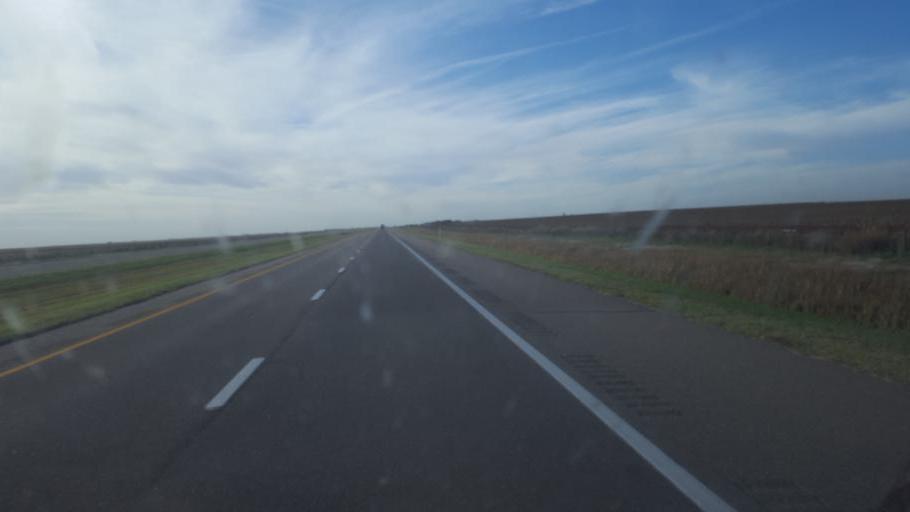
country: US
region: Kansas
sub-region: Gove County
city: Gove
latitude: 39.0340
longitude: -100.1904
